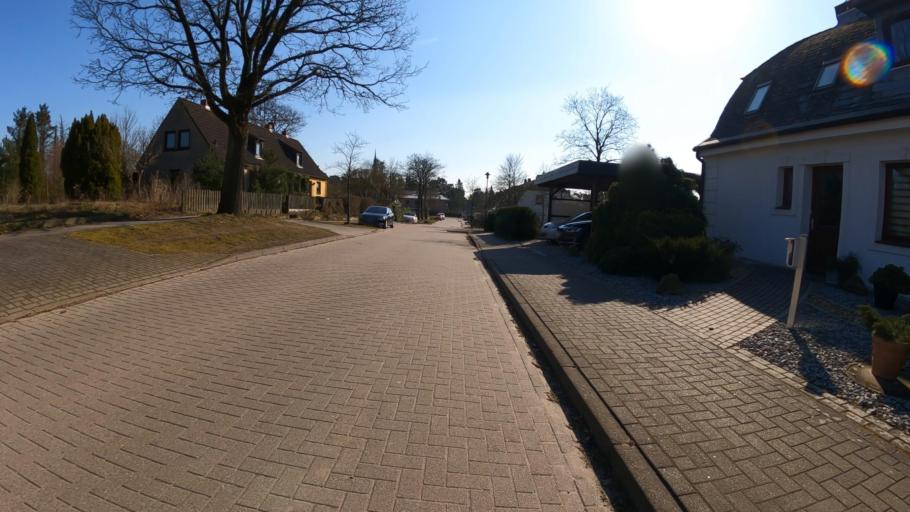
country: DE
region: Lower Saxony
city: Buchholz in der Nordheide
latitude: 53.3216
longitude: 9.8675
